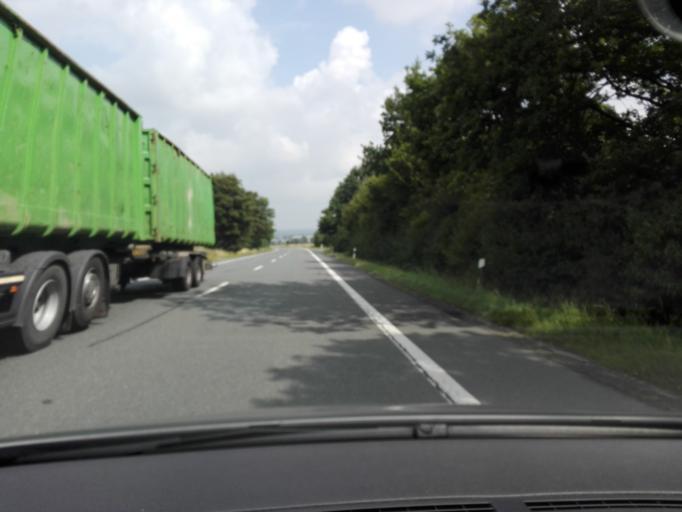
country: DE
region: North Rhine-Westphalia
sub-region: Regierungsbezirk Arnsberg
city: Frondenberg
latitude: 51.5284
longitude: 7.7702
